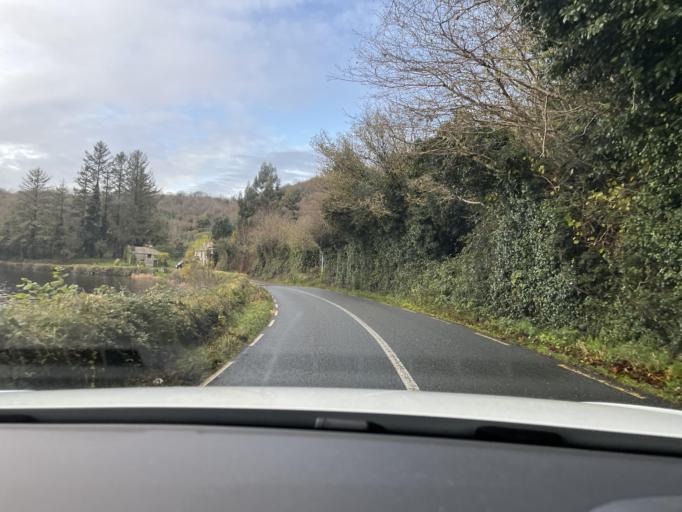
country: IE
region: Connaught
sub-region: Sligo
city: Sligo
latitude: 54.2676
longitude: -8.3444
